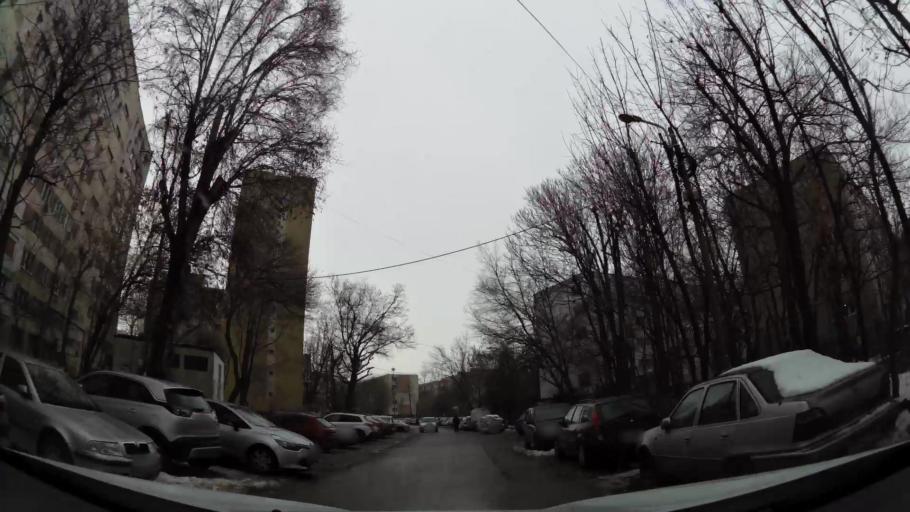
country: RO
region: Ilfov
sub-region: Comuna Chiajna
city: Rosu
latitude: 44.4210
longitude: 26.0233
